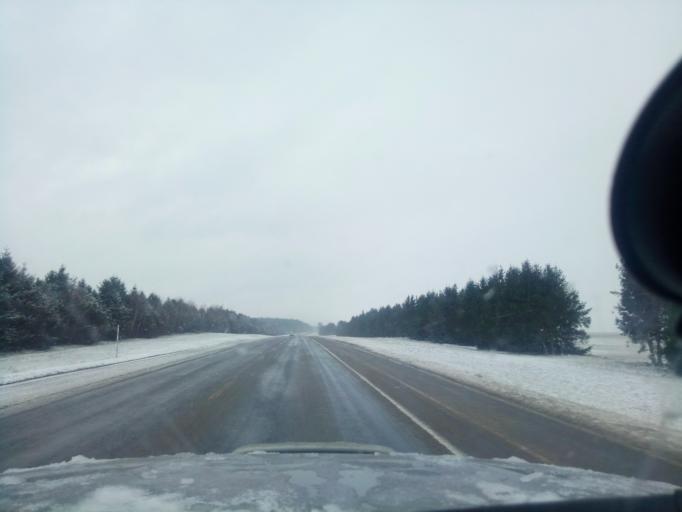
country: BY
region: Minsk
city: Haradzyeya
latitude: 53.2902
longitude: 26.5793
